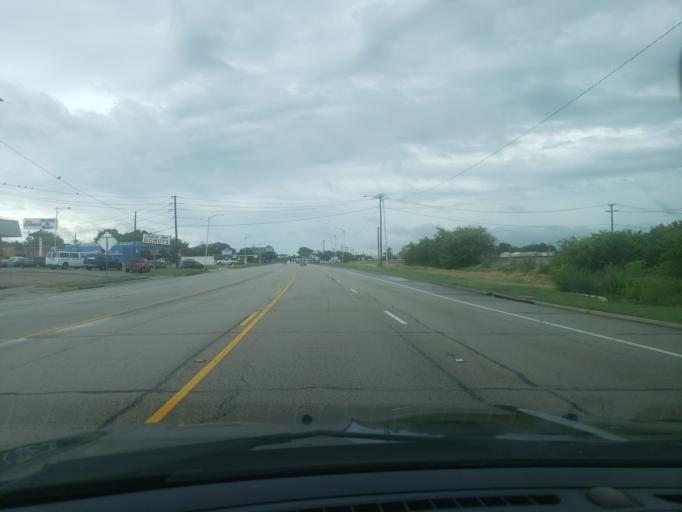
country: US
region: Texas
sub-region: Dallas County
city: Grand Prairie
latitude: 32.7427
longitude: -97.0148
